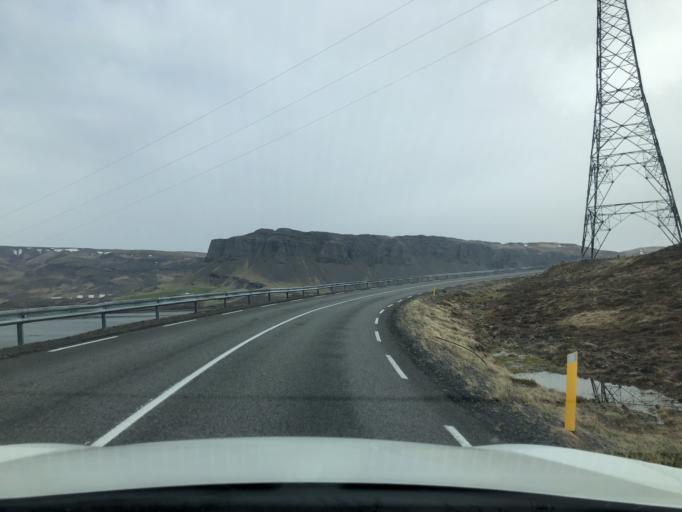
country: IS
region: Capital Region
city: Mosfellsbaer
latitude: 64.3676
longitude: -21.4178
